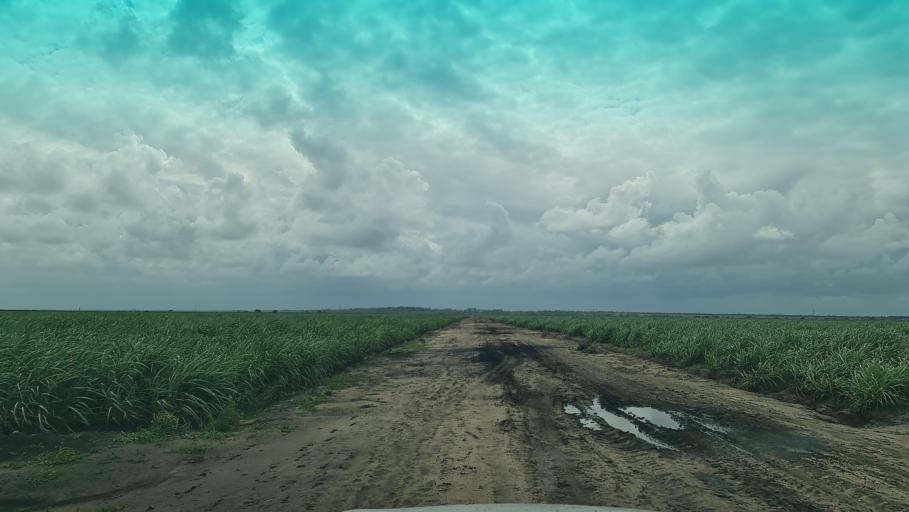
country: MZ
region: Maputo
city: Manhica
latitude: -25.4531
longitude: 32.8289
